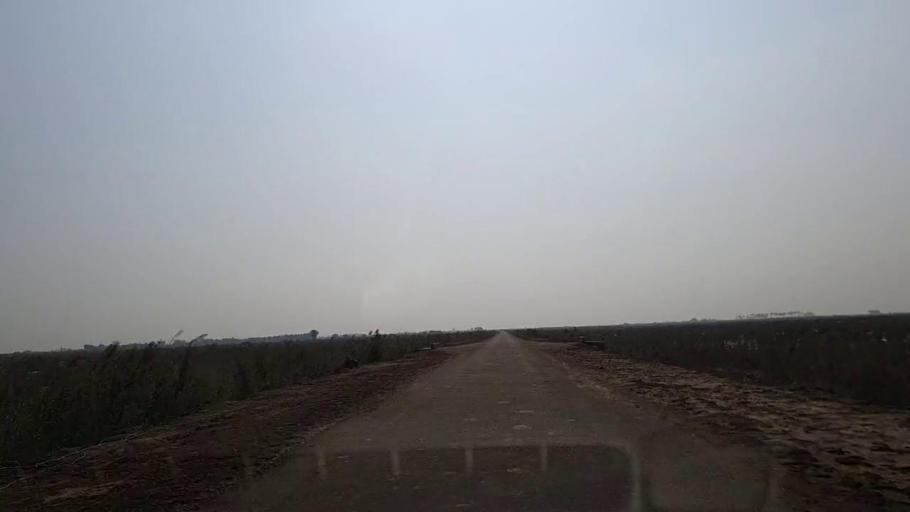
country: PK
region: Sindh
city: Gharo
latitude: 24.6660
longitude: 67.6947
